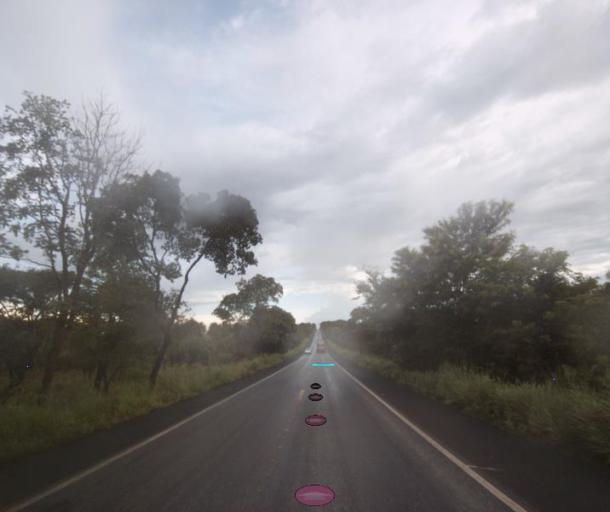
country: BR
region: Goias
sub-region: Porangatu
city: Porangatu
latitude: -13.8492
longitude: -49.0477
